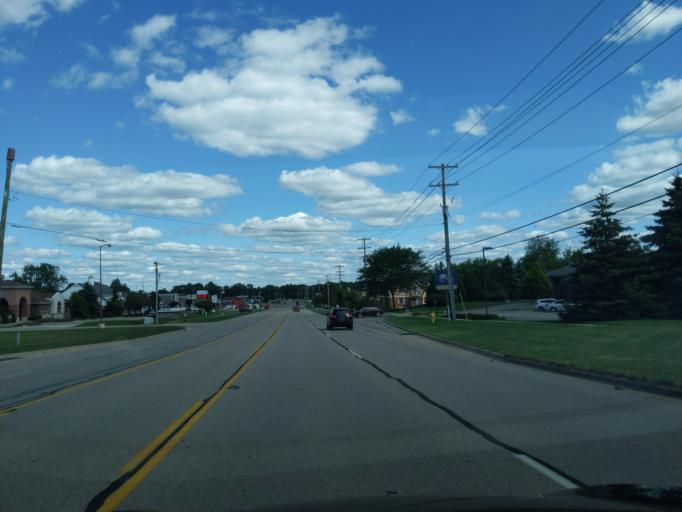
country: US
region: Michigan
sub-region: Kent County
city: Comstock Park
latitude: 43.0291
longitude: -85.6955
